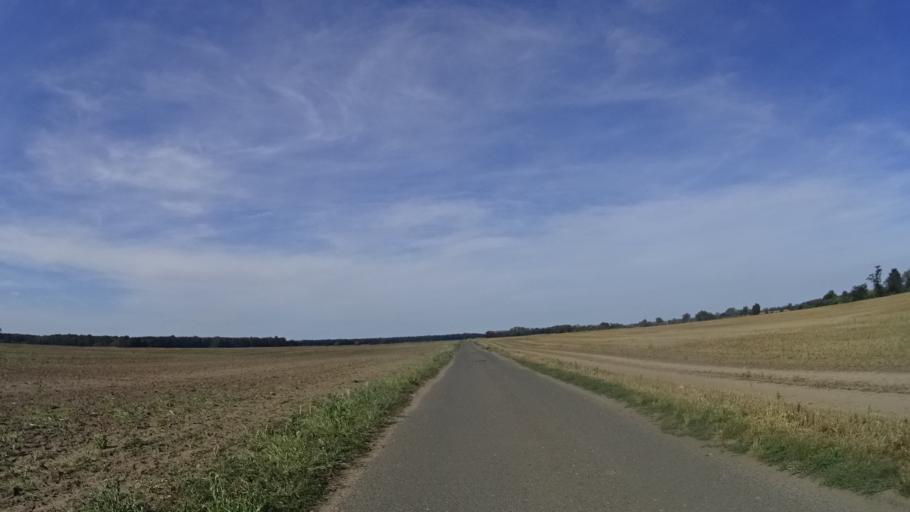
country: AT
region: Lower Austria
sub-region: Politischer Bezirk Ganserndorf
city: Durnkrut
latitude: 48.4371
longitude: 16.8733
